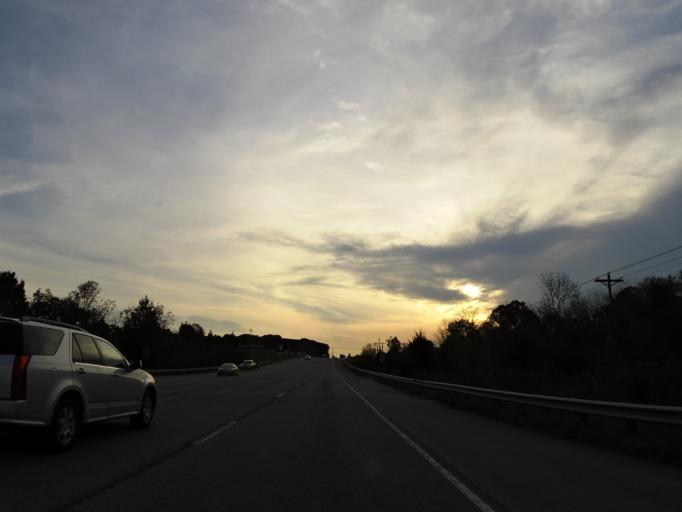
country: US
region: Tennessee
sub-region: Loudon County
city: Greenback
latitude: 35.6632
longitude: -84.1058
